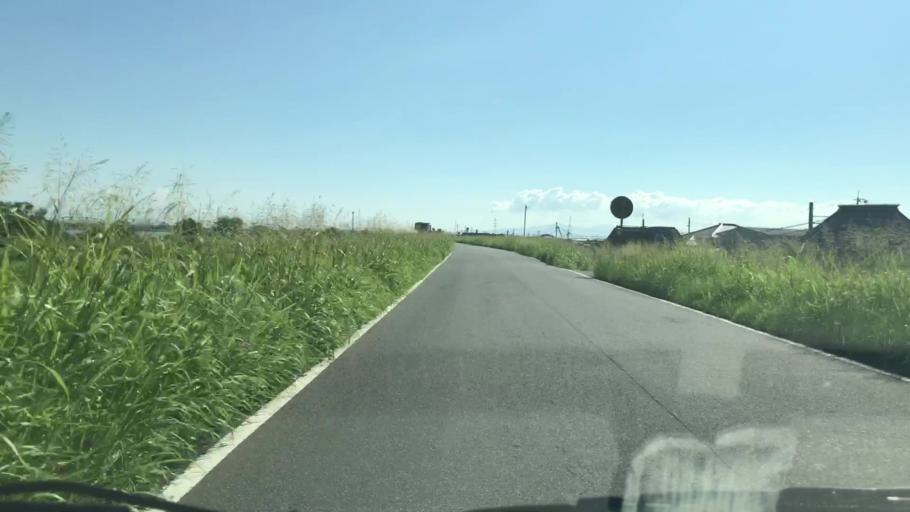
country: JP
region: Saga Prefecture
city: Kanzakimachi-kanzaki
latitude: 33.2675
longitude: 130.4215
